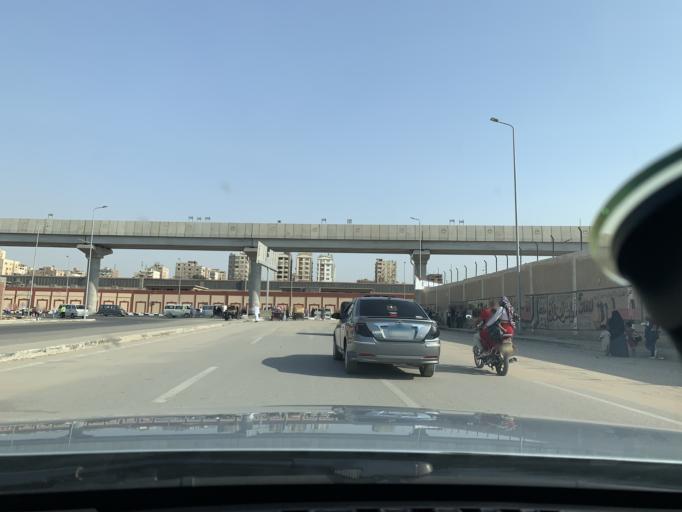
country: EG
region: Muhafazat al Qalyubiyah
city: Al Khankah
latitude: 30.1297
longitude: 31.3664
